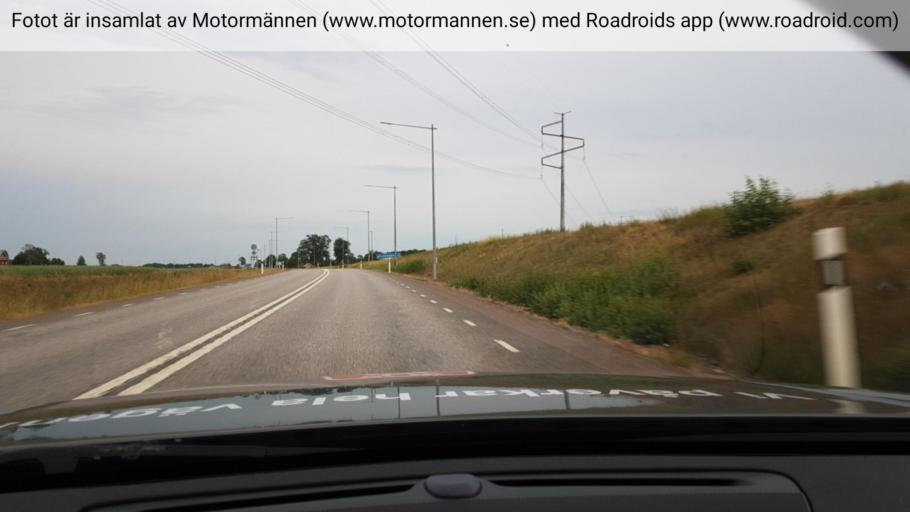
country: SE
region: OEstergoetland
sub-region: Motala Kommun
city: Borensberg
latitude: 58.5475
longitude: 15.3204
